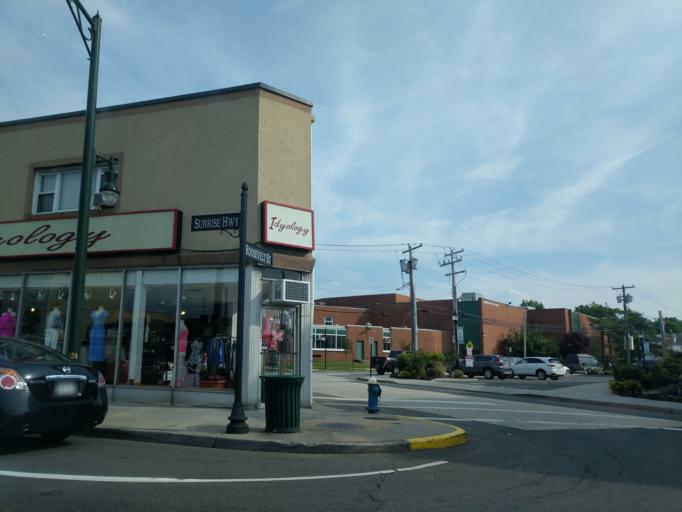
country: US
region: New York
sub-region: Nassau County
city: Lynbrook
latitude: 40.6550
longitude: -73.6729
